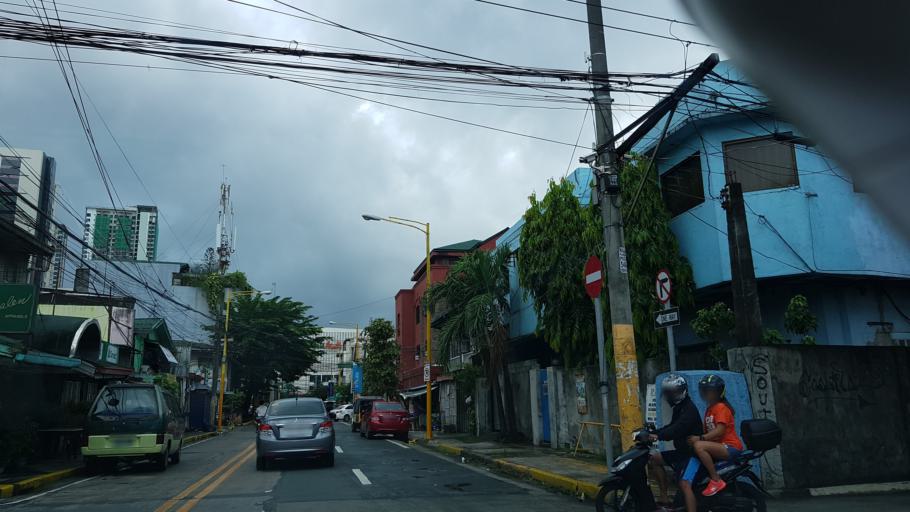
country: PH
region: Metro Manila
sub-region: Makati City
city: Makati City
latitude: 14.5698
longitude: 121.0185
